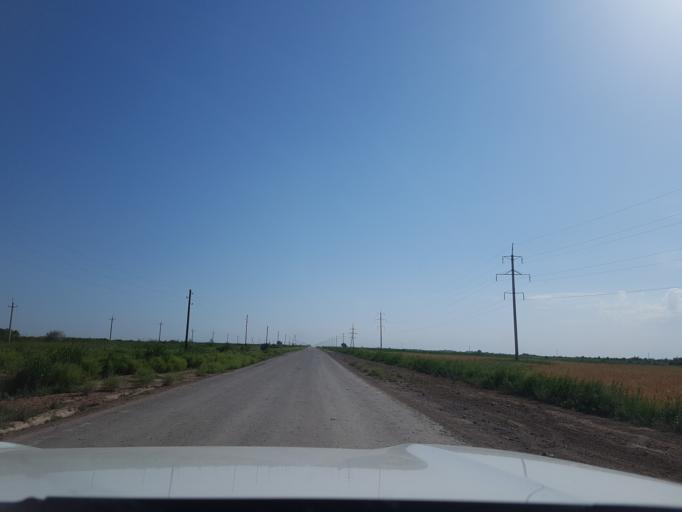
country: TM
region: Dasoguz
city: Koeneuergench
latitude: 42.1064
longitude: 58.9111
